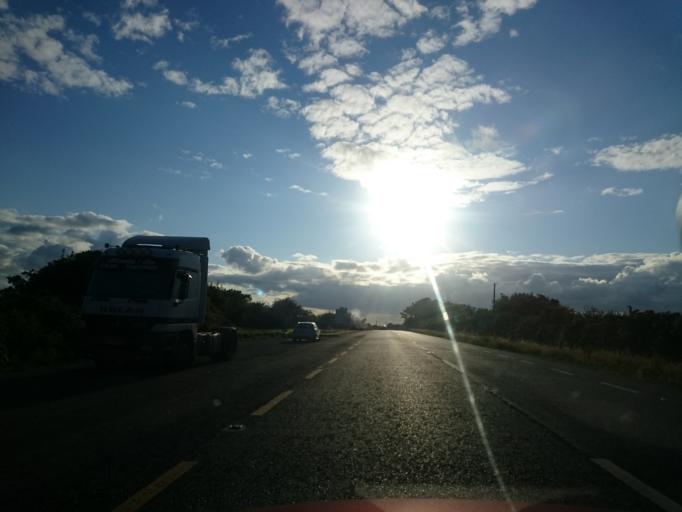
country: IE
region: Leinster
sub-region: Loch Garman
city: Ballygerry
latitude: 52.2443
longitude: -6.3656
